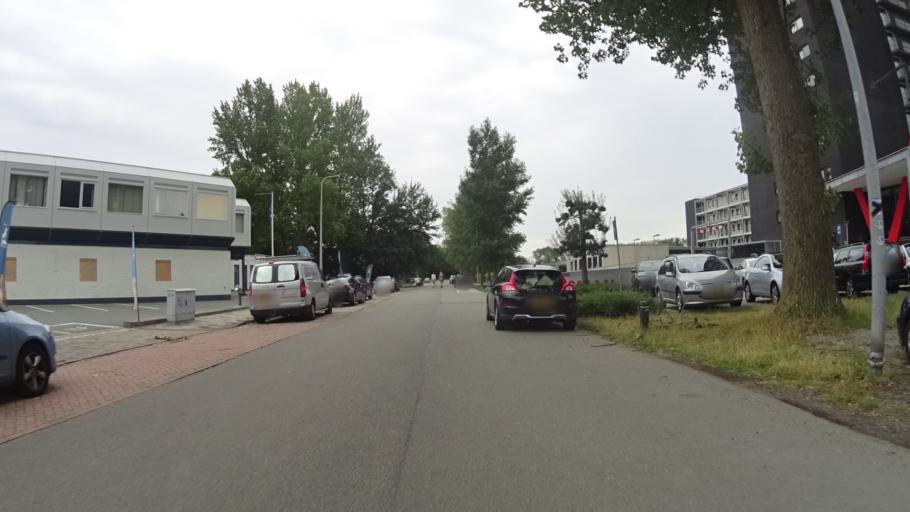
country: NL
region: Groningen
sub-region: Gemeente Groningen
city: Oosterpark
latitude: 53.2253
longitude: 6.5990
